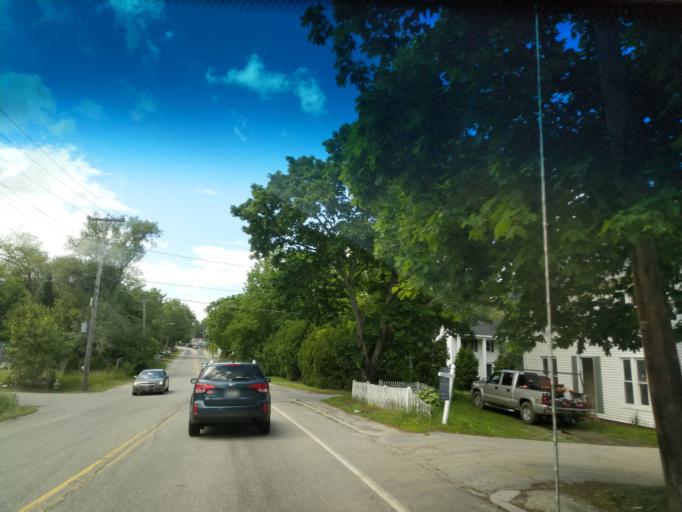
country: US
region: Maine
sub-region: Cumberland County
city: South Windham
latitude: 43.7263
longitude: -70.4227
